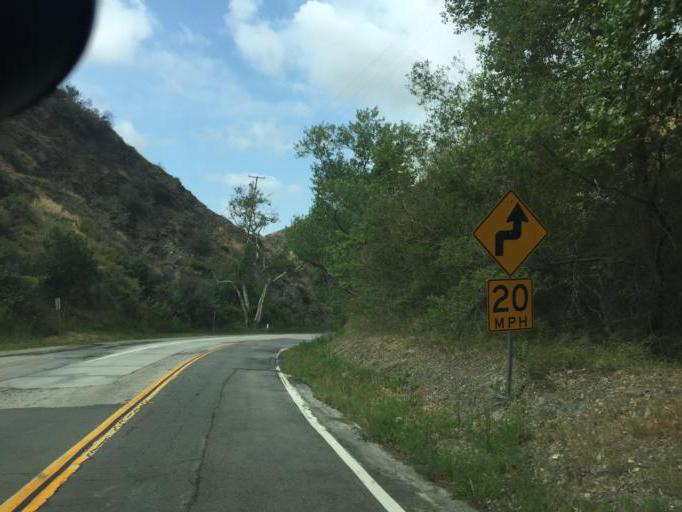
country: US
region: California
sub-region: Los Angeles County
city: Green Valley
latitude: 34.5168
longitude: -118.4477
